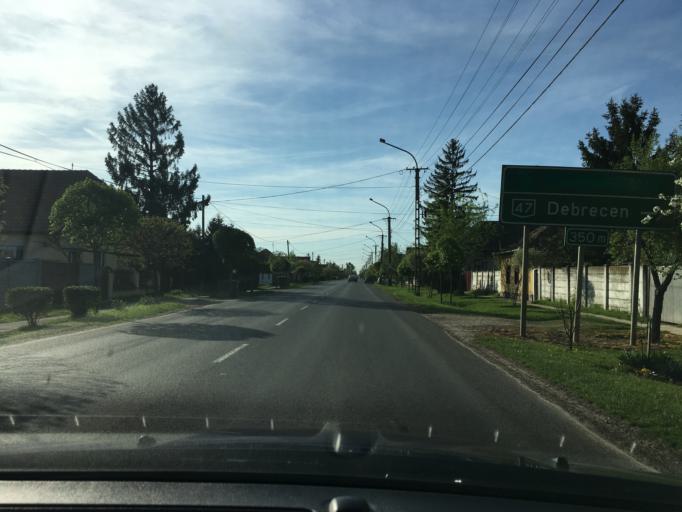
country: HU
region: Bekes
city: Korostarcsa
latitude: 46.8726
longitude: 21.0239
